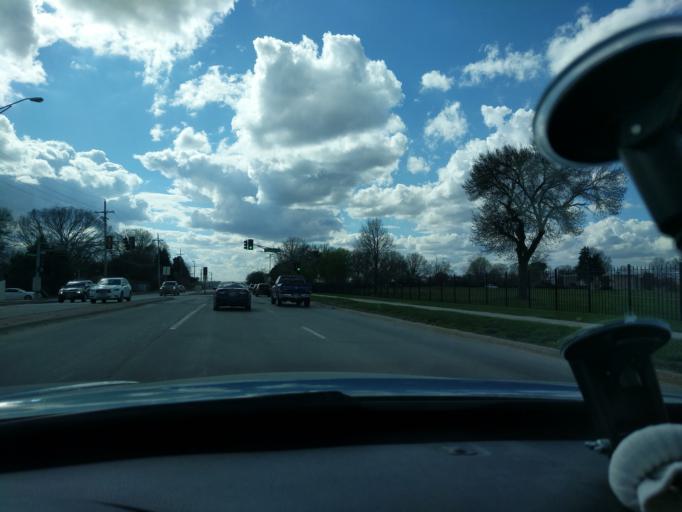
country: US
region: Nebraska
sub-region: Douglas County
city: Ralston
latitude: 41.2343
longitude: -96.0280
